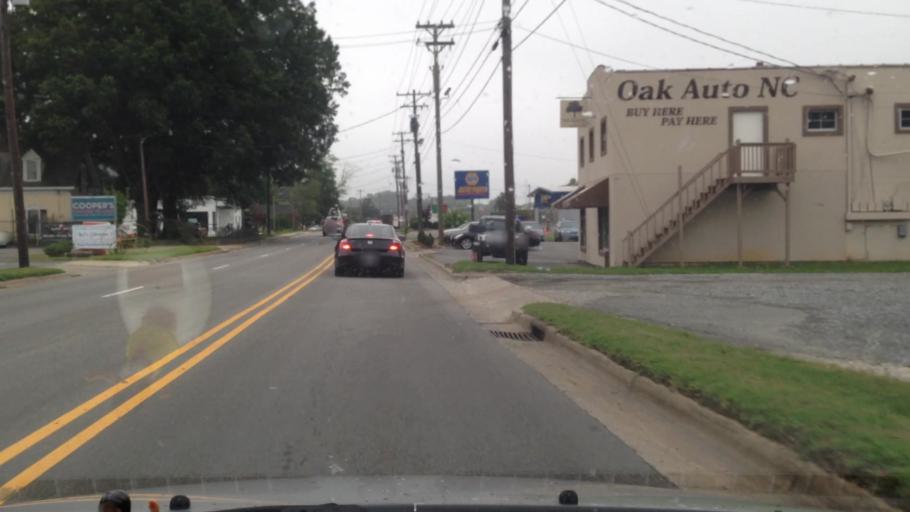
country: US
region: North Carolina
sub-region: Forsyth County
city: Kernersville
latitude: 36.1202
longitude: -80.0689
